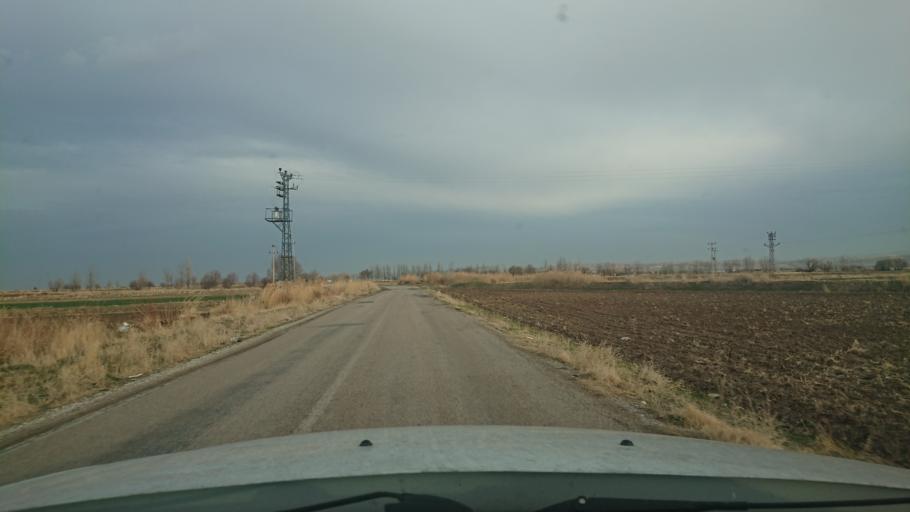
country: TR
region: Aksaray
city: Yesilova
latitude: 38.4382
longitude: 33.8381
